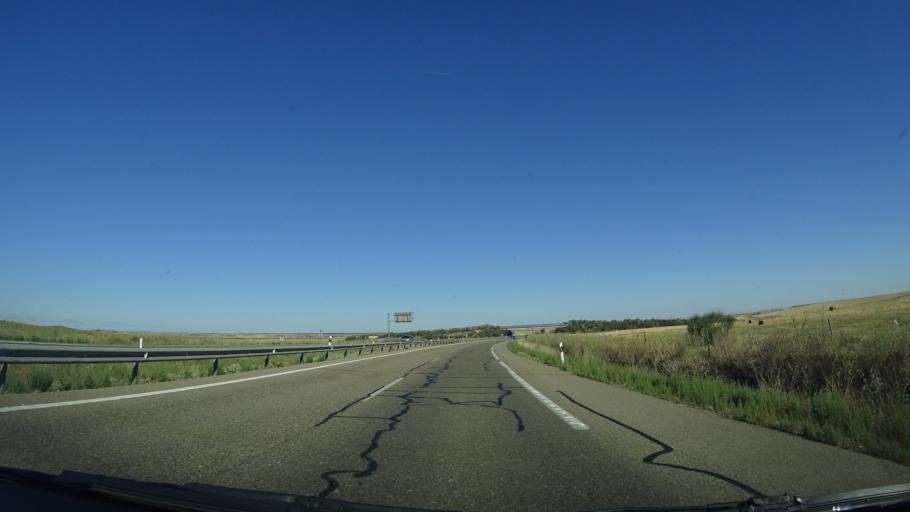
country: ES
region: Castille and Leon
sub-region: Provincia de Valladolid
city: Villardefrades
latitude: 41.7327
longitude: -5.2614
